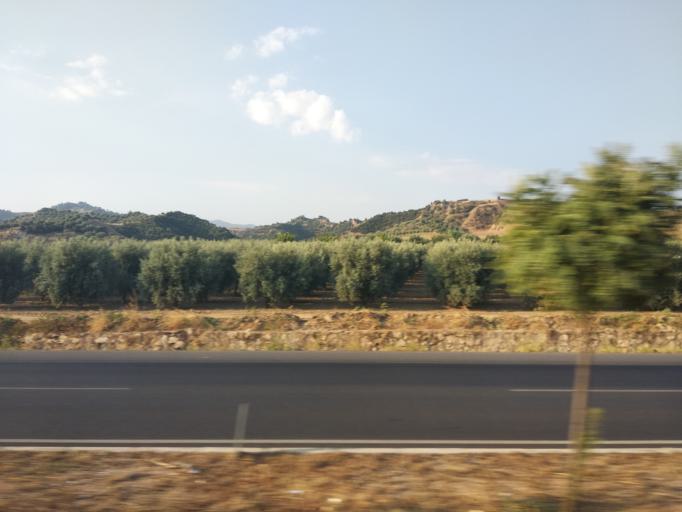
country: TR
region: Manisa
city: Ahmetli
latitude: 38.5086
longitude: 27.9841
